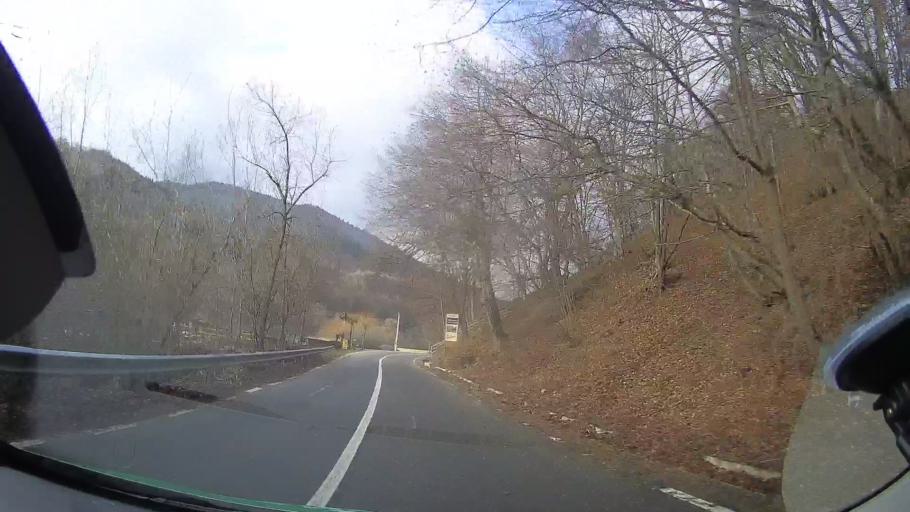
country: RO
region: Cluj
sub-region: Comuna Valea Ierii
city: Valea Ierii
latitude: 46.6386
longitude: 23.3648
